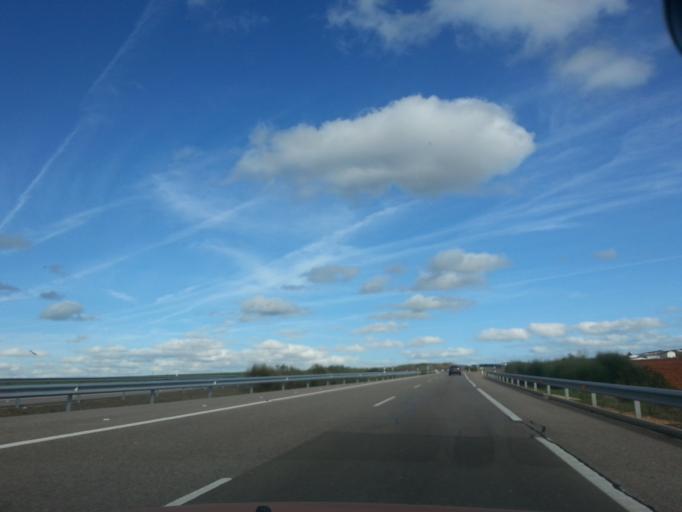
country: ES
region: Castille and Leon
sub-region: Provincia de Salamanca
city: Doninos de Salamanca
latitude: 40.9481
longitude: -5.7568
